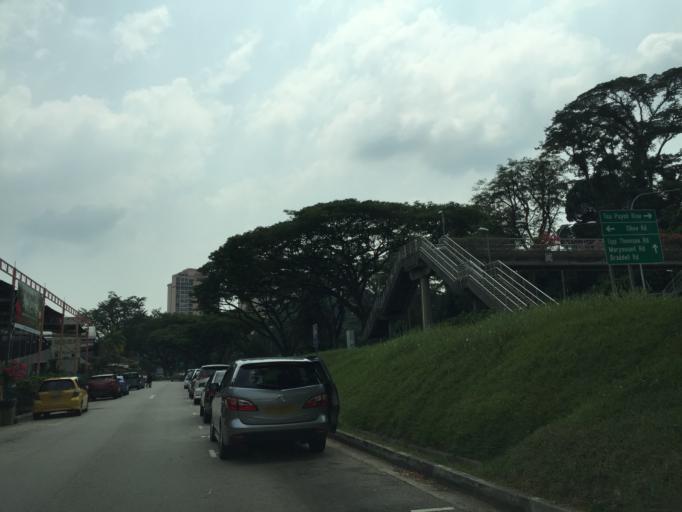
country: SG
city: Singapore
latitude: 1.3364
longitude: 103.8369
